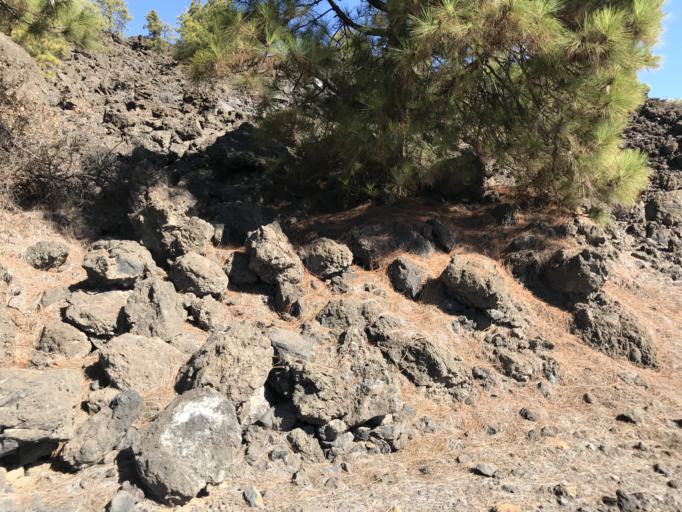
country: ES
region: Canary Islands
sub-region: Provincia de Santa Cruz de Tenerife
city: Arafo
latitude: 28.3276
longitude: -16.4348
